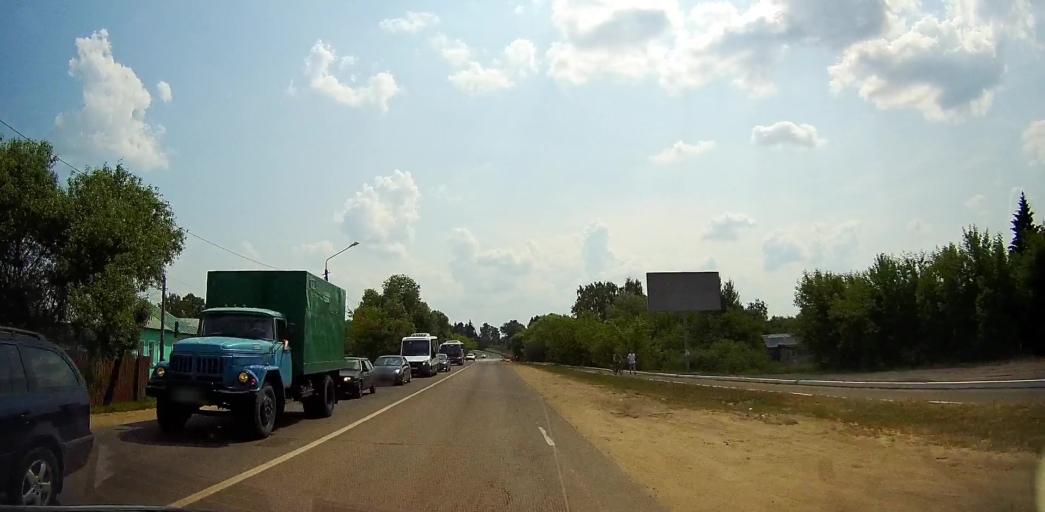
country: RU
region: Moskovskaya
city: Malino
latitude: 55.1107
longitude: 38.1778
